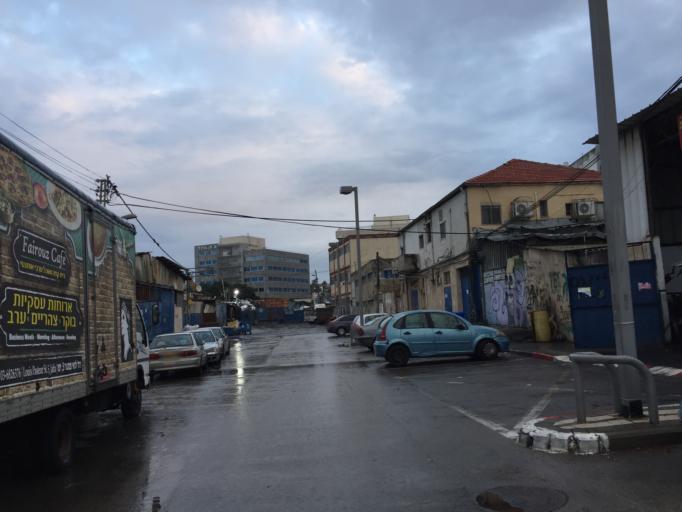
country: IL
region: Tel Aviv
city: Yafo
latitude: 32.0527
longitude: 34.7626
